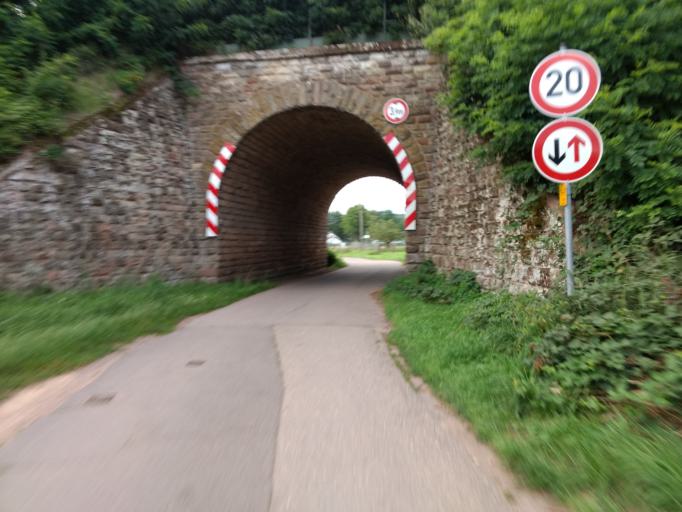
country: DE
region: Saarland
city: Dillingen
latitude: 49.3644
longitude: 6.7097
